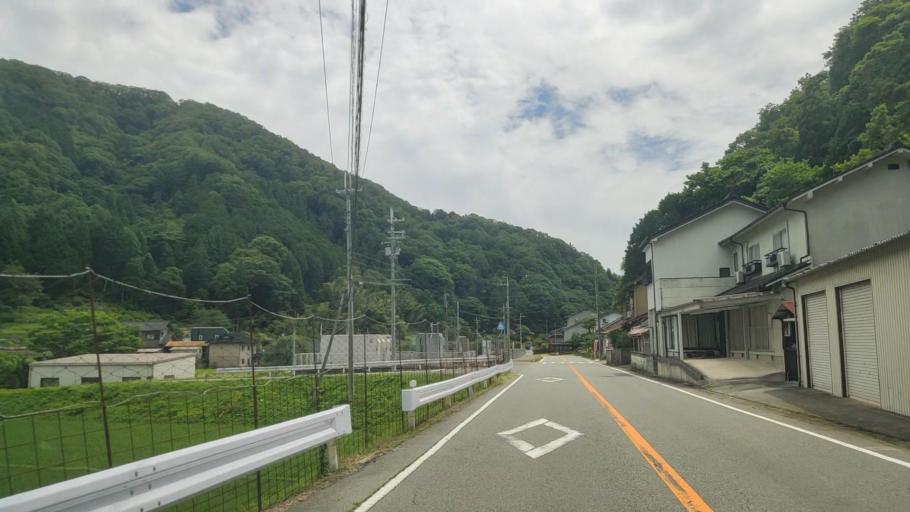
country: JP
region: Hyogo
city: Yamazakicho-nakabirose
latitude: 35.1002
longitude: 134.3628
